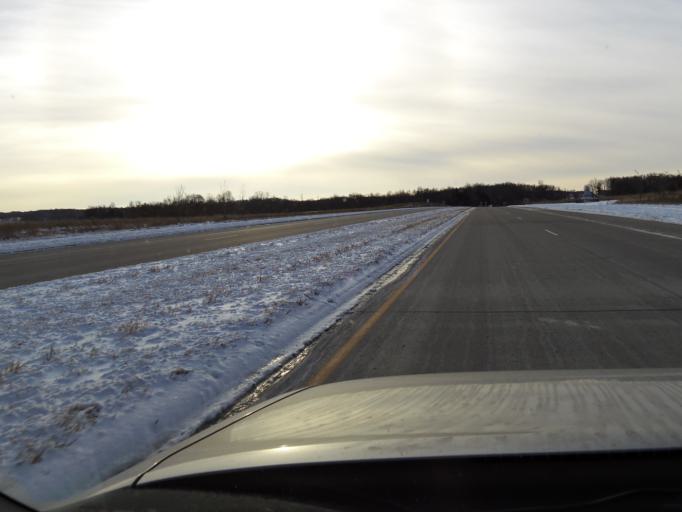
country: US
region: Minnesota
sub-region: Scott County
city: Prior Lake
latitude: 44.7539
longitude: -93.4393
